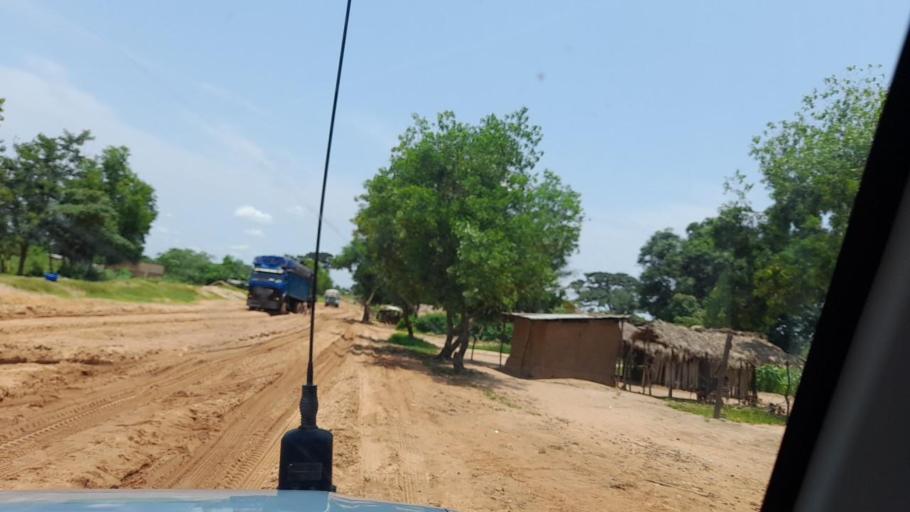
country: CD
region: Kasai-Occidental
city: Kananga
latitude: -5.9498
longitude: 22.2777
